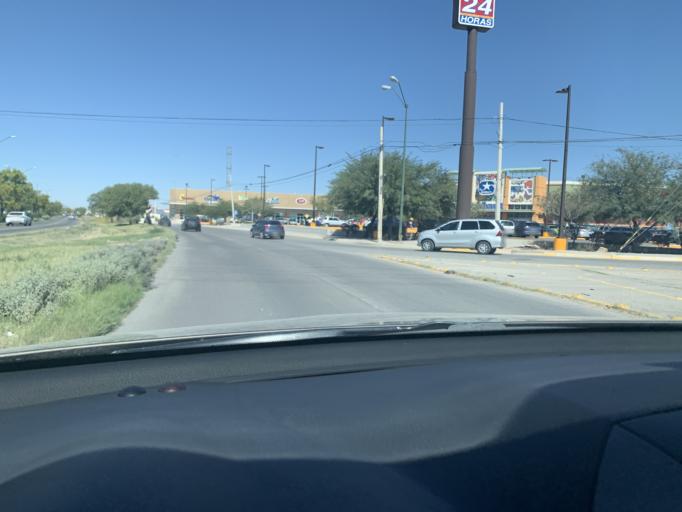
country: US
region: Texas
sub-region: El Paso County
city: Socorro
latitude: 31.6952
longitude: -106.3812
